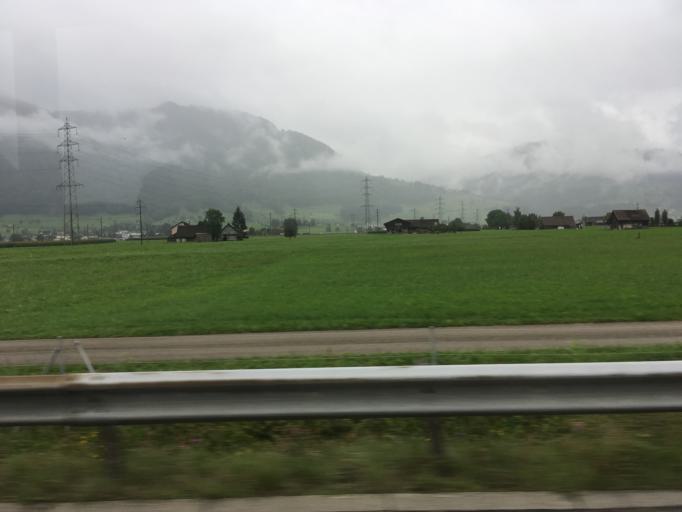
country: CH
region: Schwyz
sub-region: Bezirk March
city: Schubelbach
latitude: 47.1869
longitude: 8.9230
